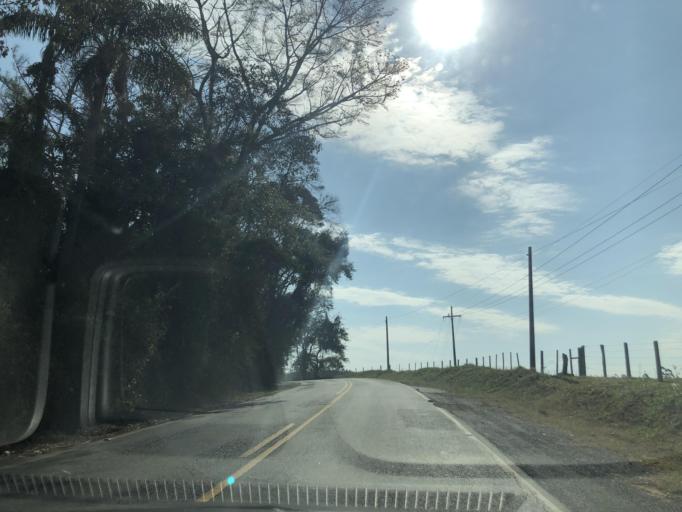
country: BR
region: Sao Paulo
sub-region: Pilar Do Sul
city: Pilar do Sul
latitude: -23.8273
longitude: -47.6762
